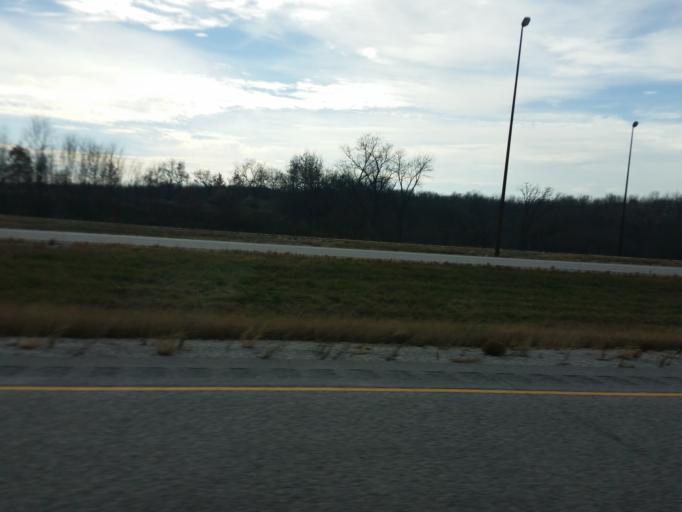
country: US
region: Illinois
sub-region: Henry County
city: Green Rock
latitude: 41.4406
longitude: -90.3346
